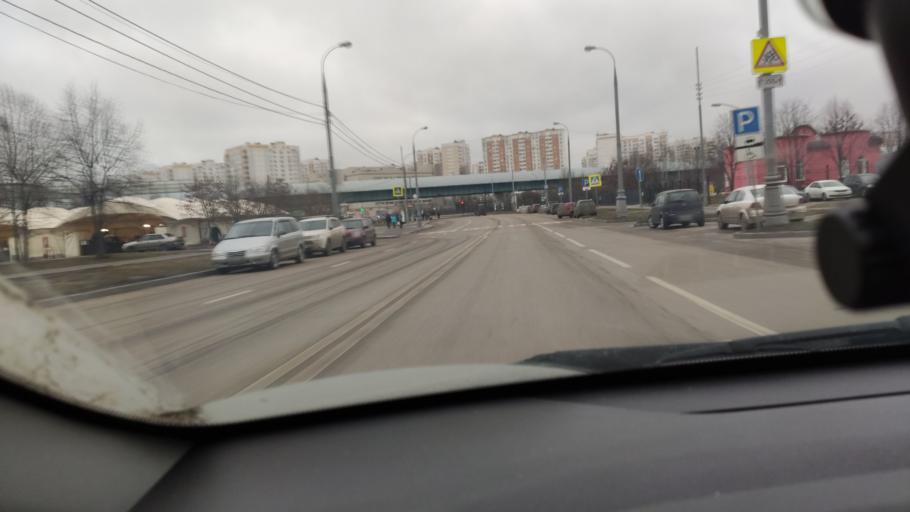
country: RU
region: Moskovskaya
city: Shcherbinka
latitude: 55.5408
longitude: 37.5335
